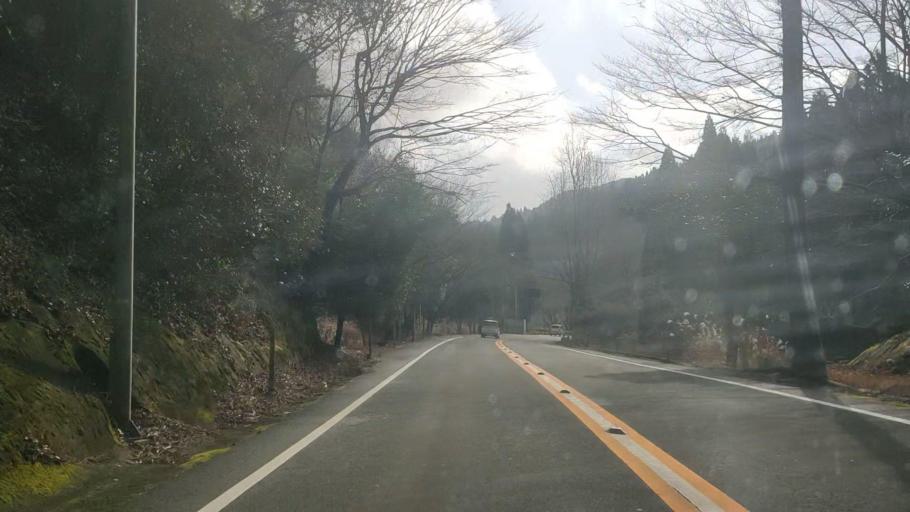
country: JP
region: Kumamoto
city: Hitoyoshi
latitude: 32.1062
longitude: 130.8050
